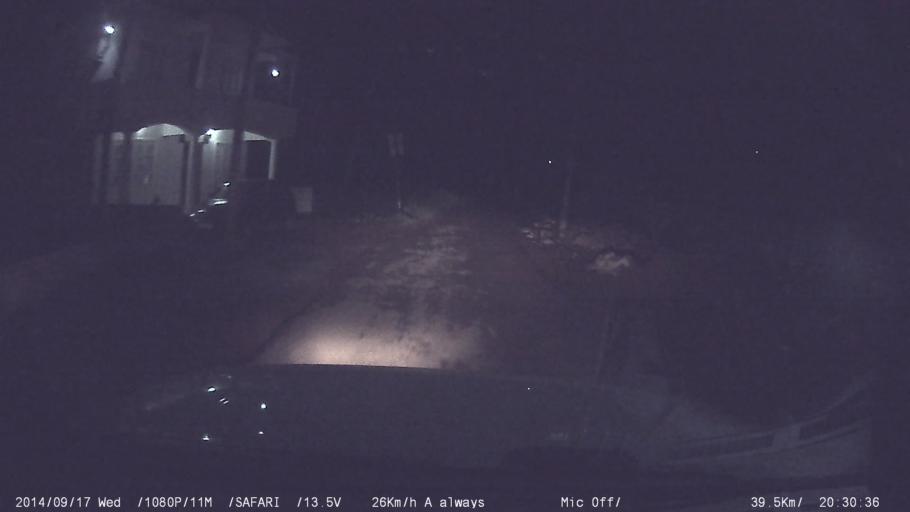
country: IN
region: Kerala
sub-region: Kottayam
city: Kottayam
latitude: 9.6373
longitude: 76.5396
